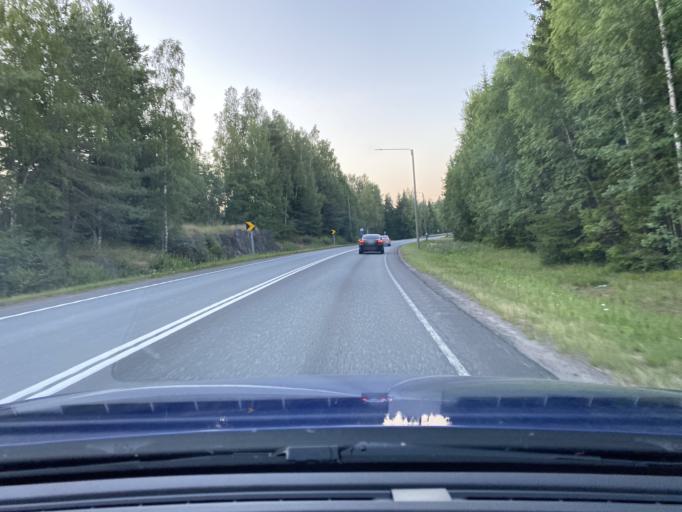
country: FI
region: Pirkanmaa
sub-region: Luoteis-Pirkanmaa
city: Ikaalinen
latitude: 61.8480
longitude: 22.9305
